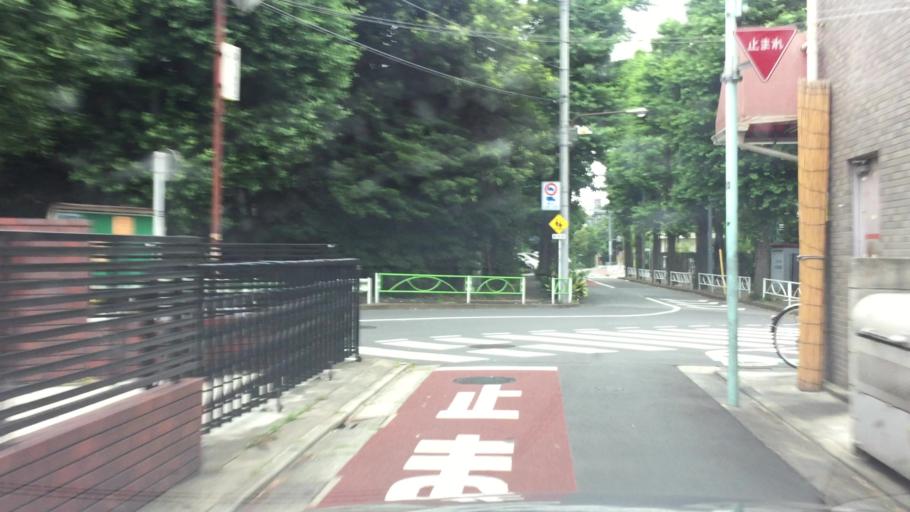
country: JP
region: Tokyo
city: Tokyo
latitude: 35.6459
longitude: 139.6894
